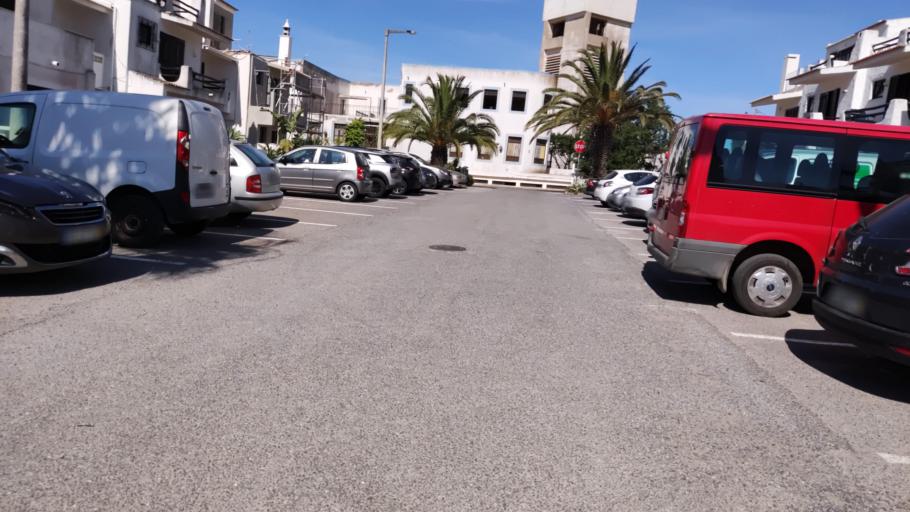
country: PT
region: Faro
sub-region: Lagos
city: Lagos
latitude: 37.0931
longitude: -8.6819
